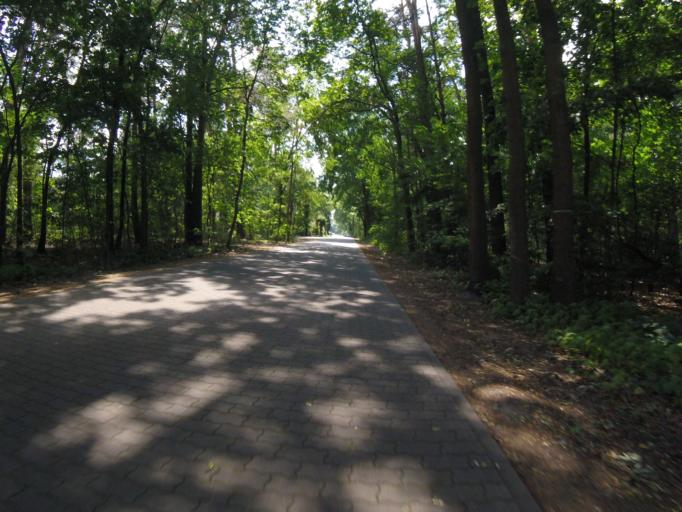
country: DE
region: Brandenburg
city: Bestensee
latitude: 52.2448
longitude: 13.6495
